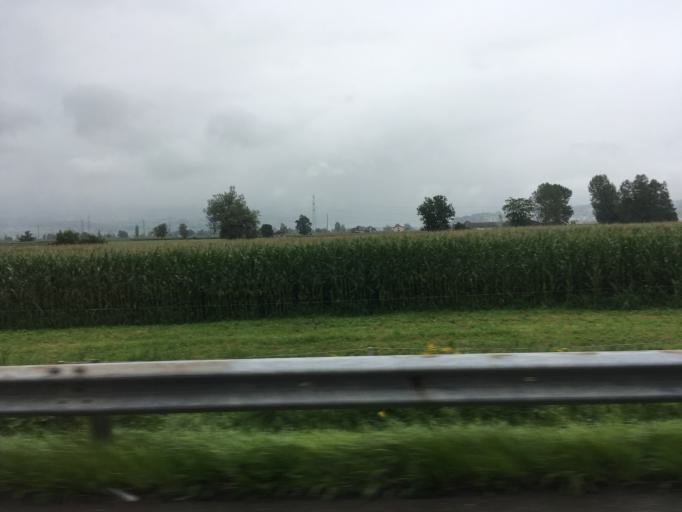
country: CH
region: Schwyz
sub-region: Bezirk March
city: Tuggen
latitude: 47.1960
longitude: 8.9712
